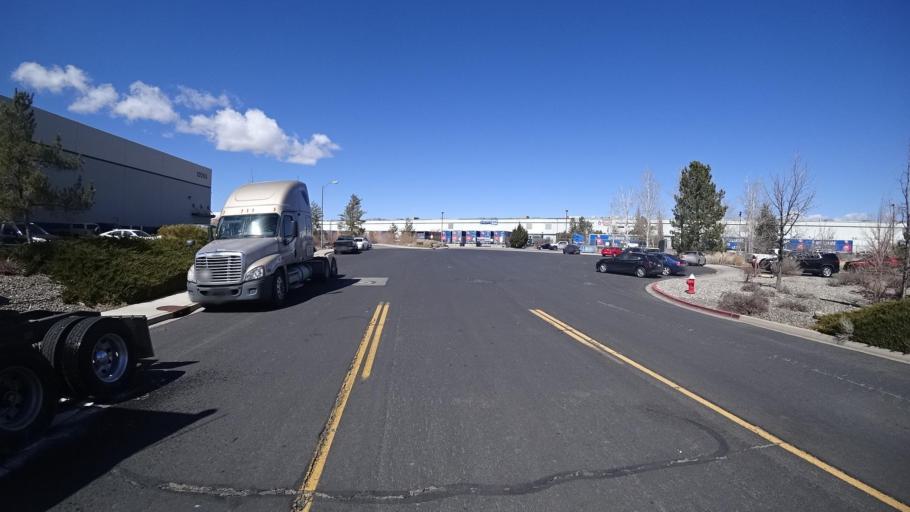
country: US
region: Nevada
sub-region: Washoe County
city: Lemmon Valley
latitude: 39.6475
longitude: -119.8626
